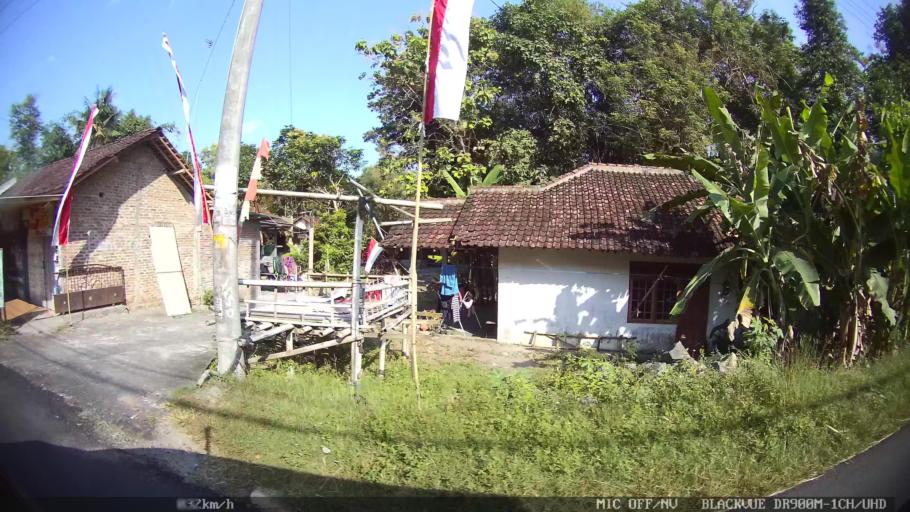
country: ID
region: Daerah Istimewa Yogyakarta
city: Kasihan
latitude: -7.8228
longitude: 110.2737
